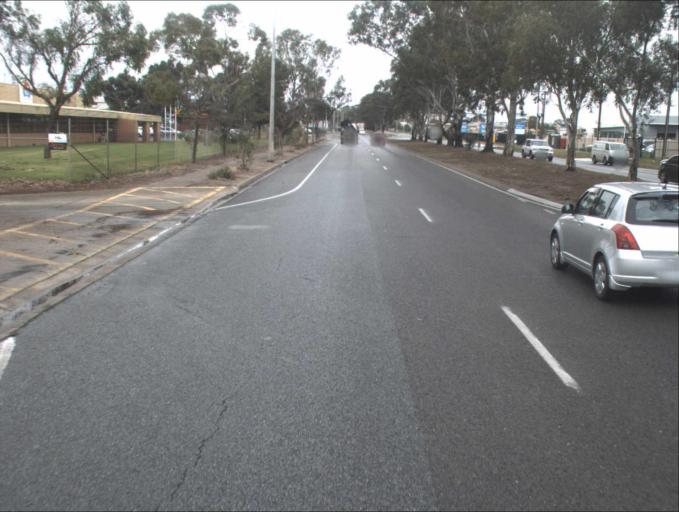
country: AU
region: South Australia
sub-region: Port Adelaide Enfield
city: Enfield
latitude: -34.8416
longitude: 138.5910
